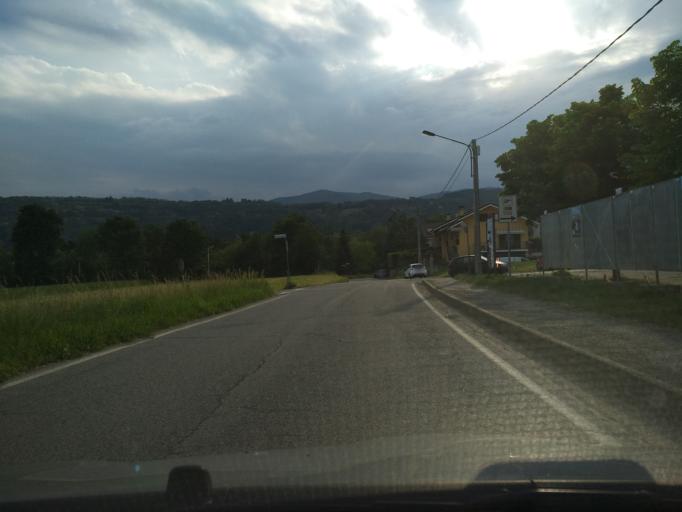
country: IT
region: Piedmont
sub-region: Provincia di Torino
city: Roletto
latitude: 44.9198
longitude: 7.3377
